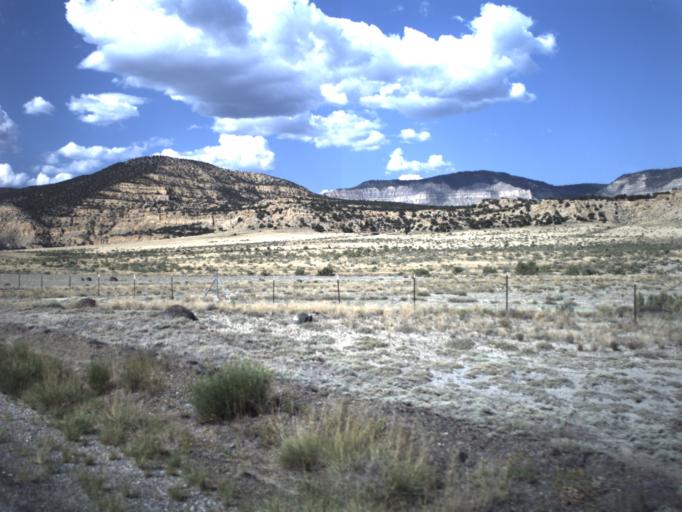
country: US
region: Utah
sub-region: Emery County
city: Ferron
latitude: 38.7987
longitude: -111.3429
